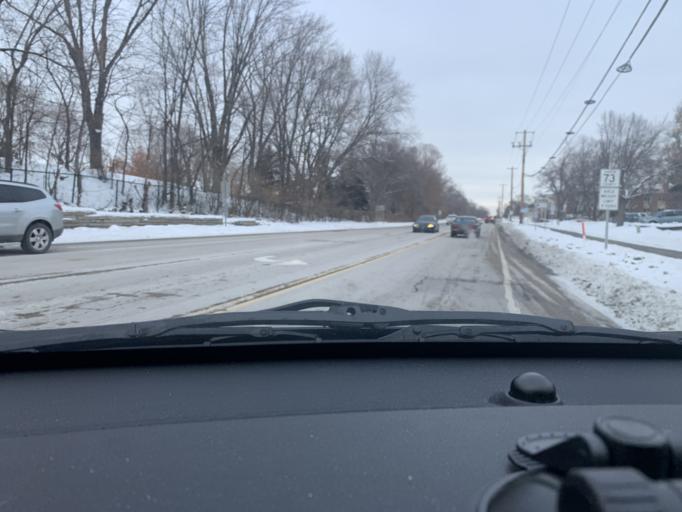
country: US
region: Minnesota
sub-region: Dakota County
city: South Saint Paul
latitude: 44.8837
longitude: -93.0703
